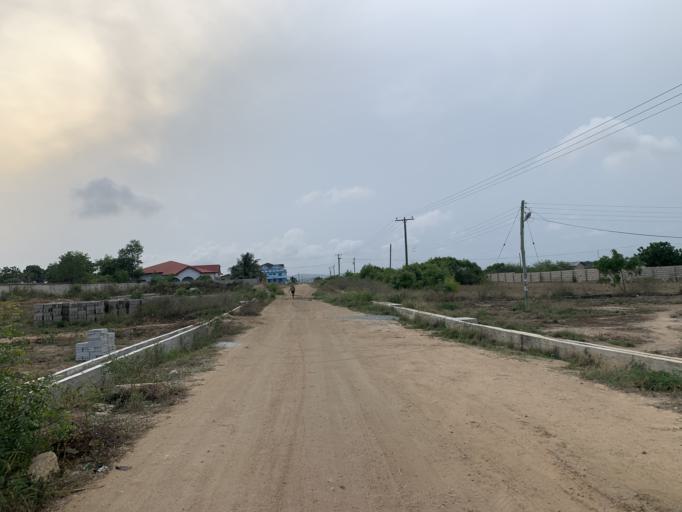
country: GH
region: Central
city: Winneba
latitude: 5.3819
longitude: -0.6242
